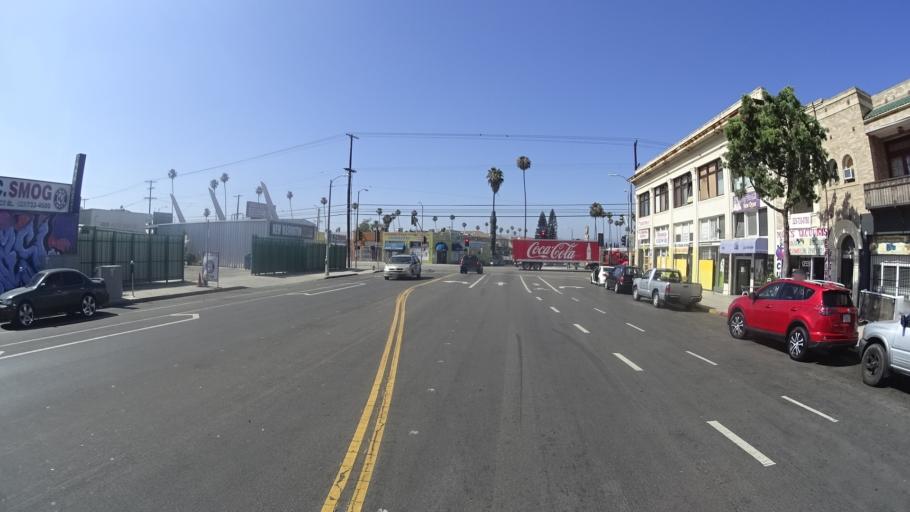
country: US
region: California
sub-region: Los Angeles County
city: Hollywood
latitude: 34.0468
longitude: -118.3211
